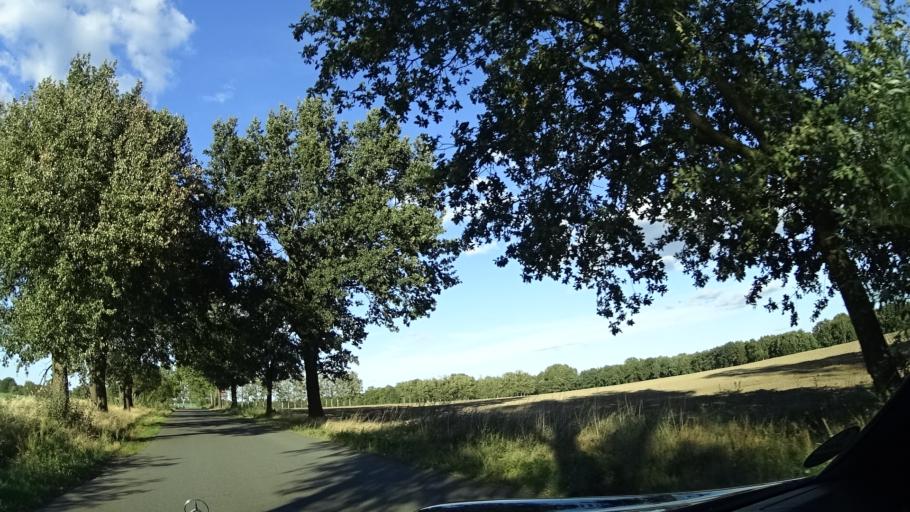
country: DE
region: Brandenburg
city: Neuruppin
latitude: 52.9522
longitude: 12.7605
